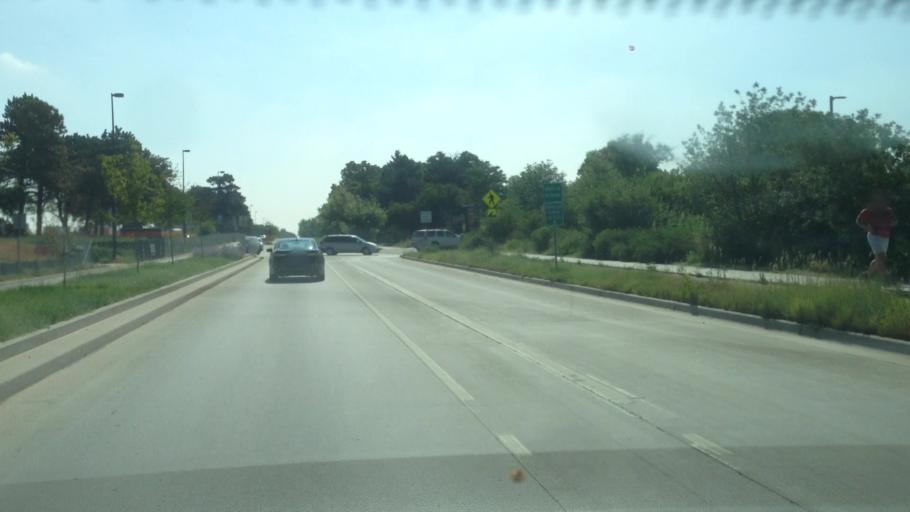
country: US
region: Colorado
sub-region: Denver County
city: Denver
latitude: 39.7512
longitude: -104.9499
